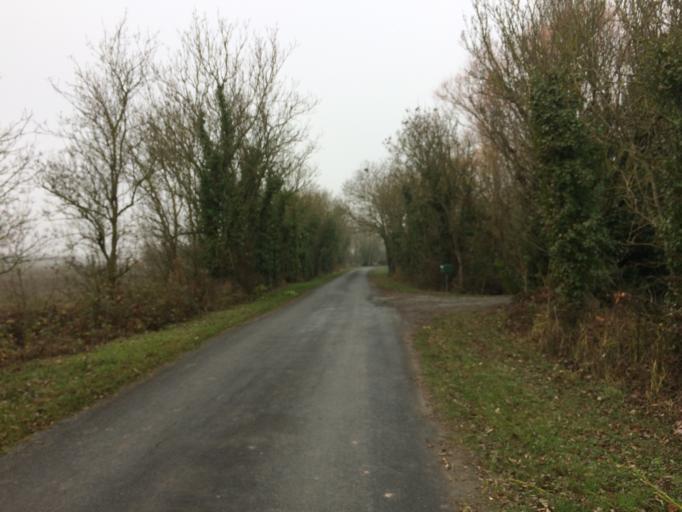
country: FR
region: Pays de la Loire
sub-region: Departement de la Vendee
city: Chaille-les-Marais
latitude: 46.3769
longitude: -1.0204
